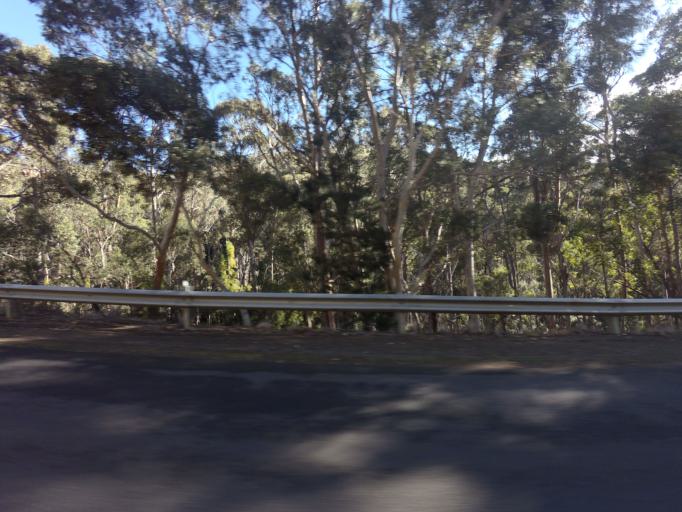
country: AU
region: Tasmania
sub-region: Glenorchy
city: Berriedale
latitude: -42.8256
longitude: 147.2093
